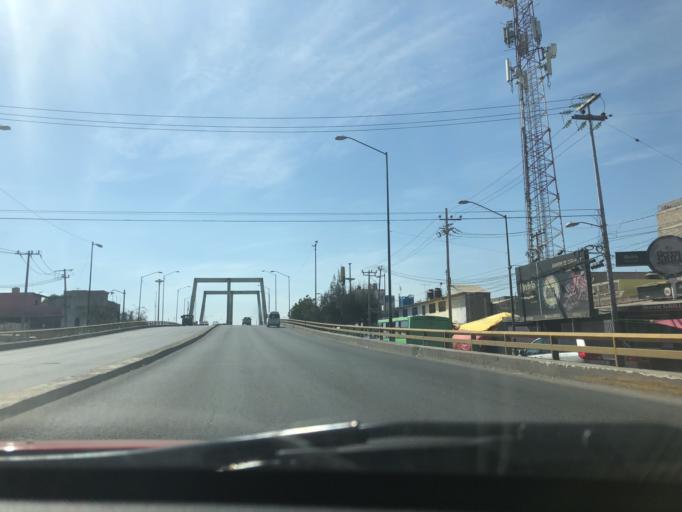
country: MX
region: Mexico
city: Ciudad Nezahualcoyotl
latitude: 19.3880
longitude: -99.0359
